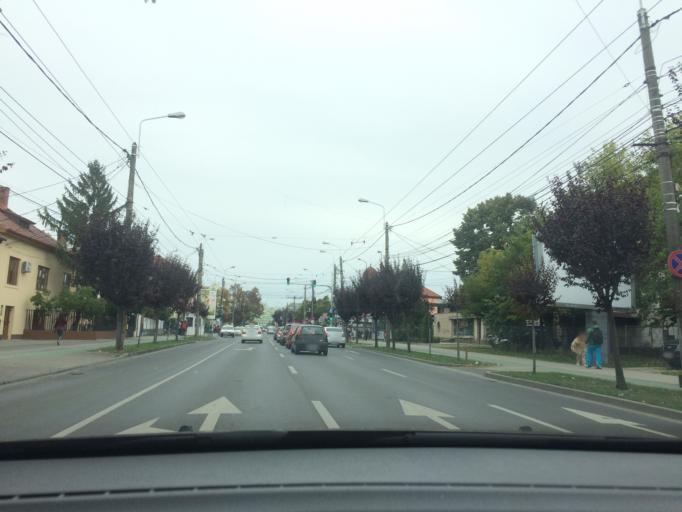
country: RO
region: Timis
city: Timisoara
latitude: 45.7443
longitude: 21.2365
